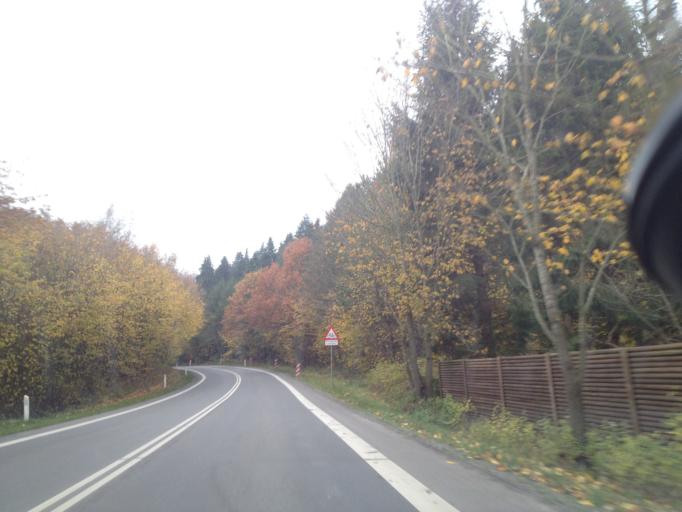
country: DK
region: South Denmark
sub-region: Nordfyns Kommune
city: Sonderso
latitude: 55.4420
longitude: 10.2027
